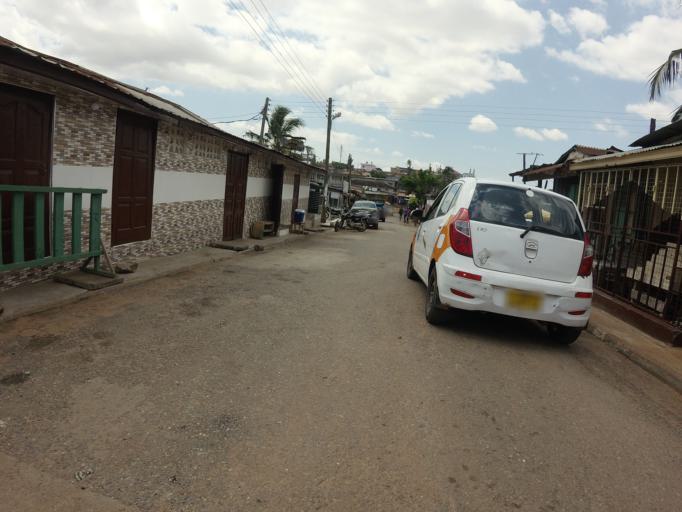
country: GH
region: Greater Accra
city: Accra
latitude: 5.5818
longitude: -0.2032
